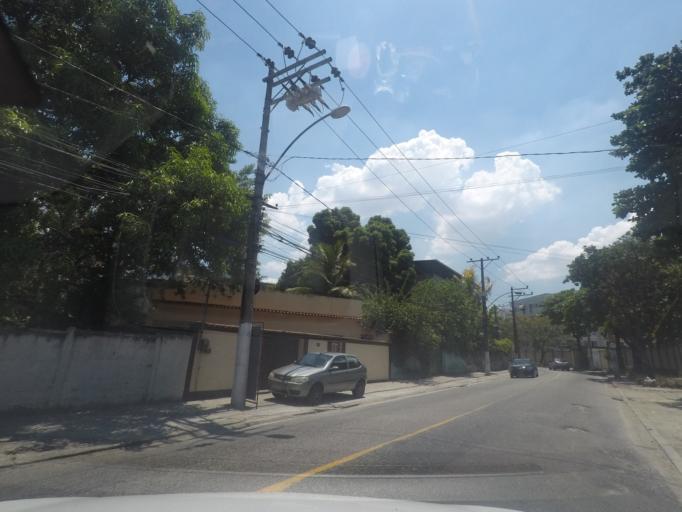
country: BR
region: Rio de Janeiro
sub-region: Duque De Caxias
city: Duque de Caxias
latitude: -22.8184
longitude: -43.3032
